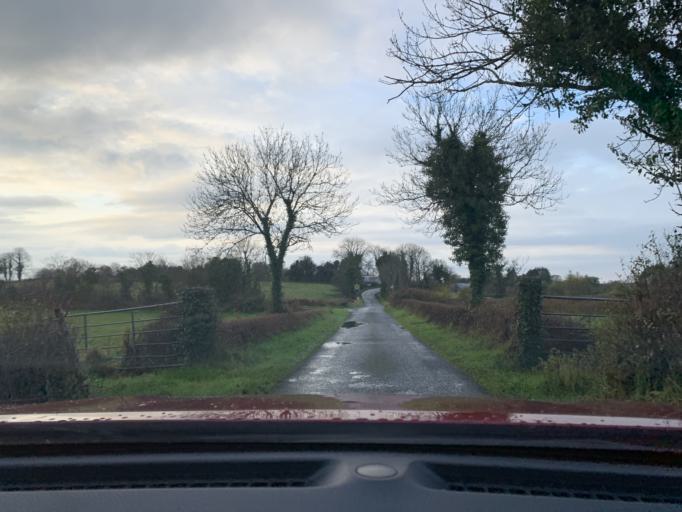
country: IE
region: Connaught
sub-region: Sligo
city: Ballymote
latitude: 54.0410
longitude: -8.5514
